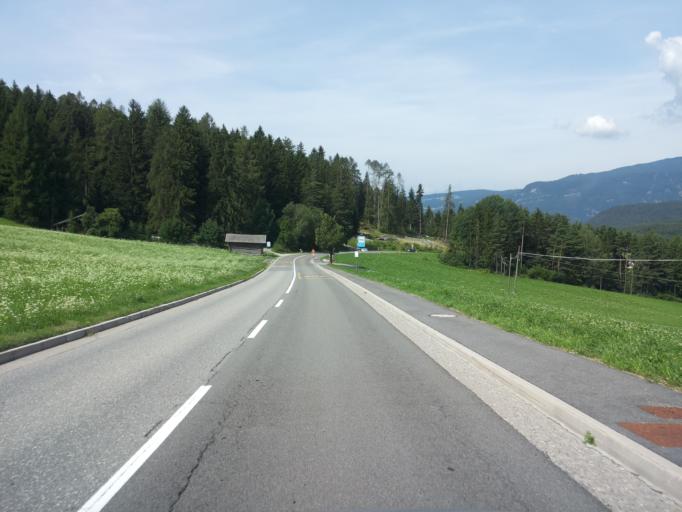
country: IT
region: Trentino-Alto Adige
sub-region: Bolzano
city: Castelrotto
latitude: 46.5713
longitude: 11.5859
